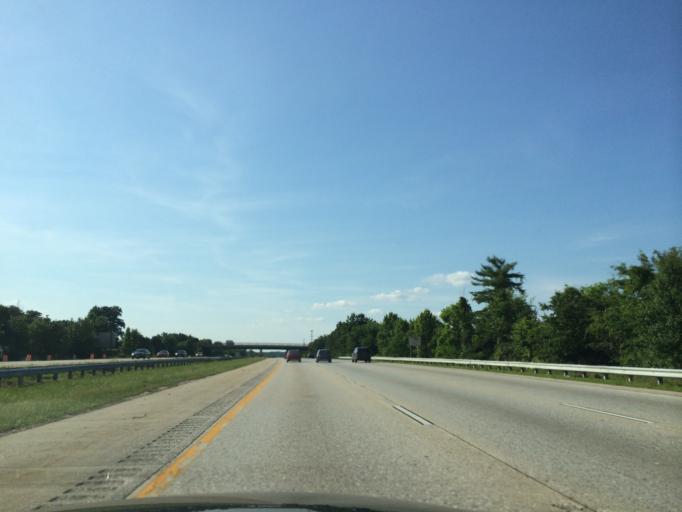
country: US
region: Maryland
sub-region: Anne Arundel County
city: South Gate
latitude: 39.1078
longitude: -76.6309
